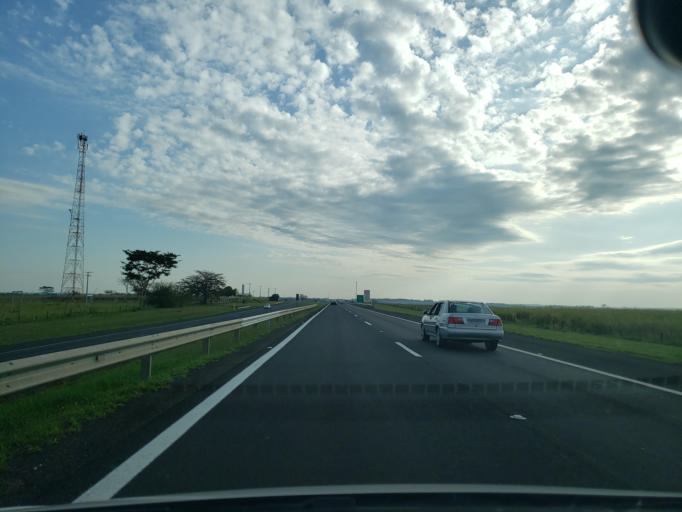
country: BR
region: Sao Paulo
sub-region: Guararapes
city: Guararapes
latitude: -21.2059
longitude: -50.6328
